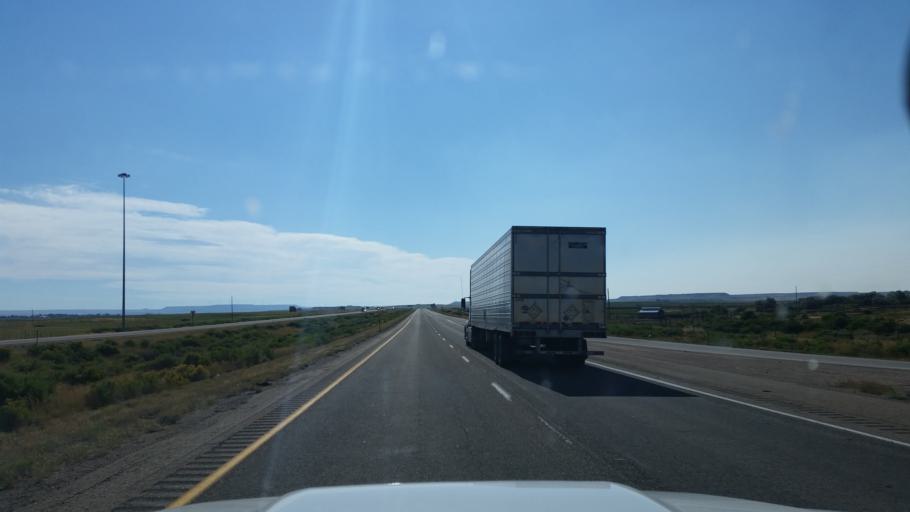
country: US
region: Wyoming
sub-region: Uinta County
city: Lyman
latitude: 41.3662
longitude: -110.3037
